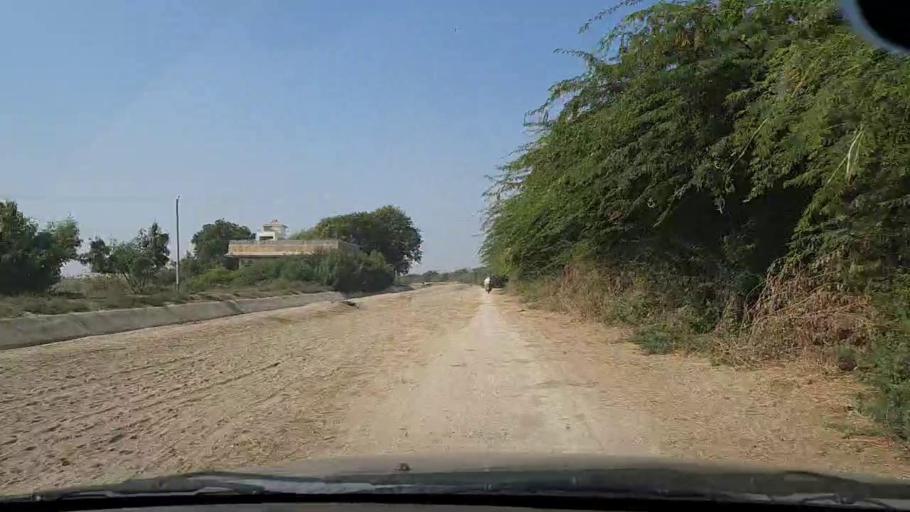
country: PK
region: Sindh
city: Chuhar Jamali
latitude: 24.4263
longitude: 67.8138
